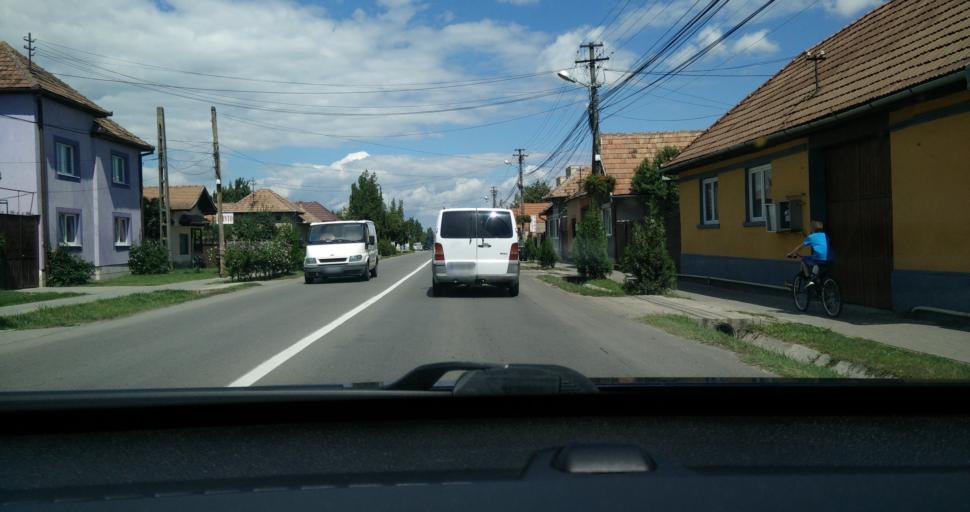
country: RO
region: Alba
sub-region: Municipiul Sebes
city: Sebes
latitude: 45.9633
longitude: 23.5574
